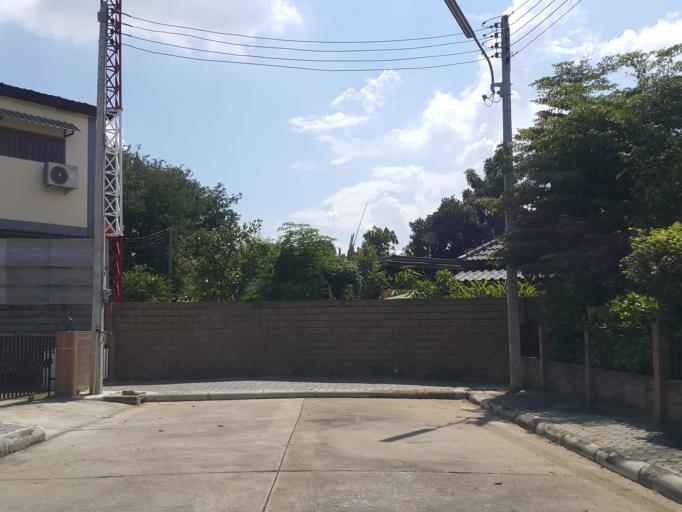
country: TH
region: Chiang Mai
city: Saraphi
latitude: 18.7558
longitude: 99.0560
